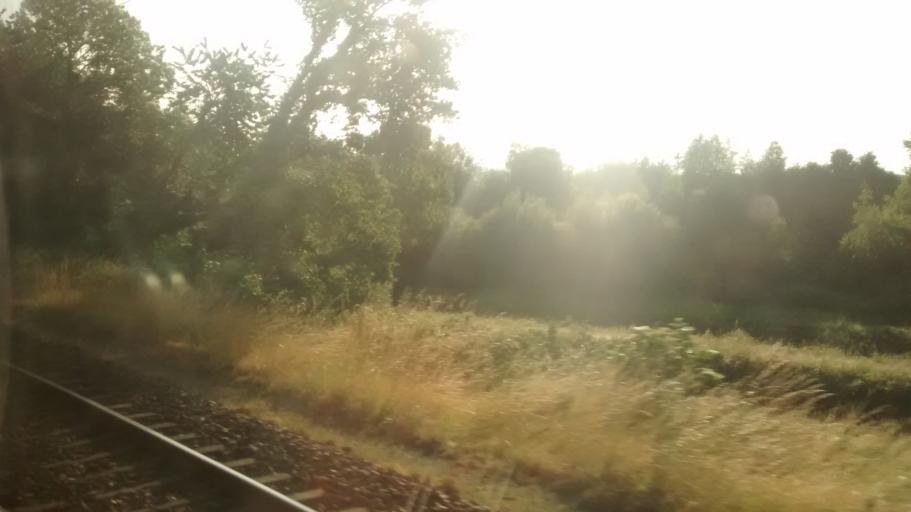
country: FR
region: Brittany
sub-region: Departement d'Ille-et-Vilaine
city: Saint-Didier
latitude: 48.1109
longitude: -1.3177
